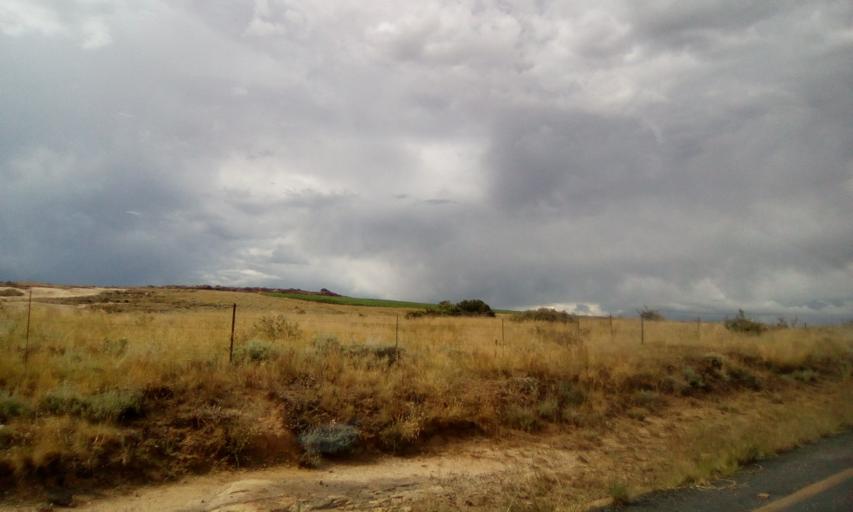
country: ZA
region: Orange Free State
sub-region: Thabo Mofutsanyana District Municipality
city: Ladybrand
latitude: -29.2453
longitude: 27.4463
